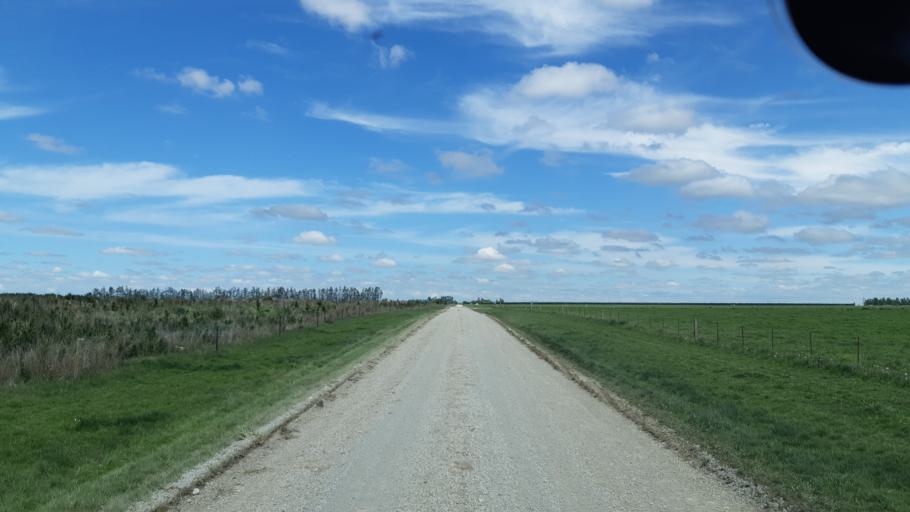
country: NZ
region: Canterbury
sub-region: Ashburton District
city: Methven
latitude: -43.7051
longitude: 171.4601
